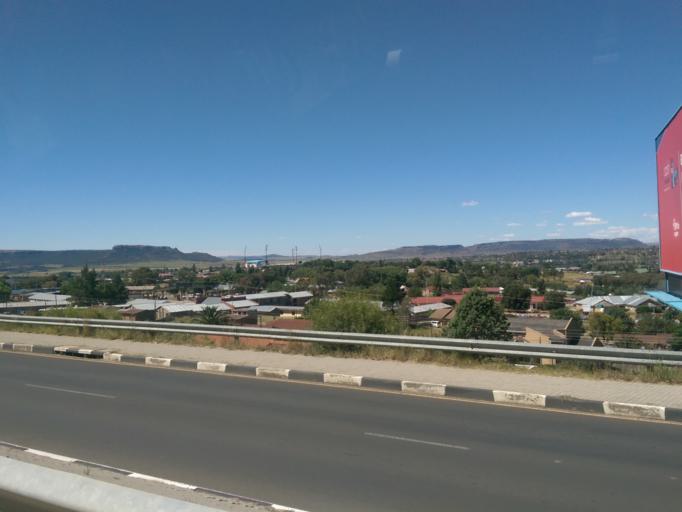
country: LS
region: Maseru
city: Maseru
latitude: -29.3237
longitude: 27.4959
